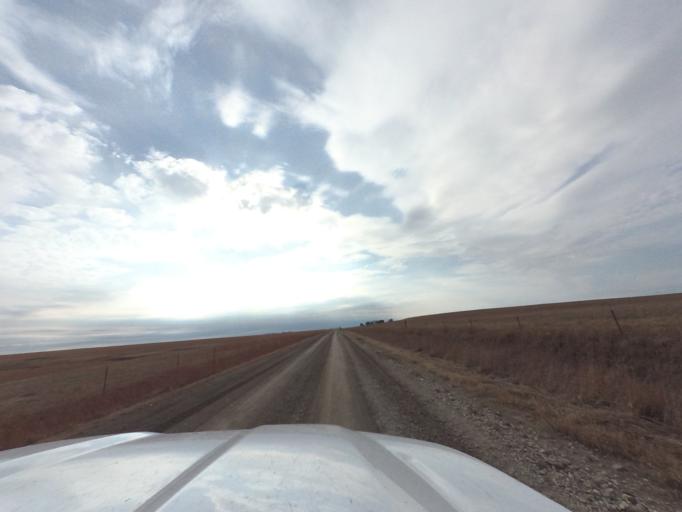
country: US
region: Kansas
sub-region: Chase County
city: Cottonwood Falls
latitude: 38.2221
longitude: -96.7307
